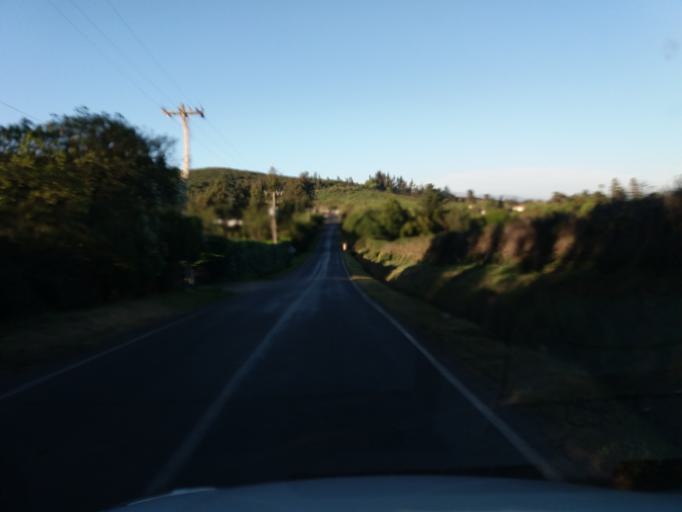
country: CL
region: Valparaiso
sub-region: Provincia de Quillota
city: Quillota
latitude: -32.8979
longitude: -71.2971
